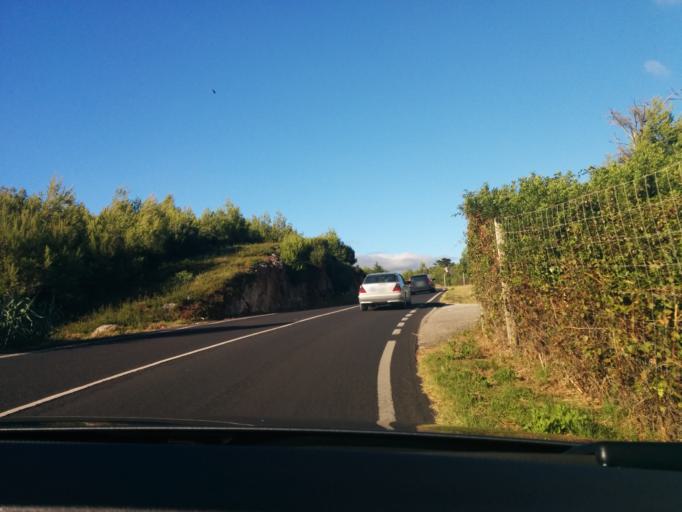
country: PT
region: Lisbon
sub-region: Cascais
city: Alcabideche
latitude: 38.7384
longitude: -9.4557
